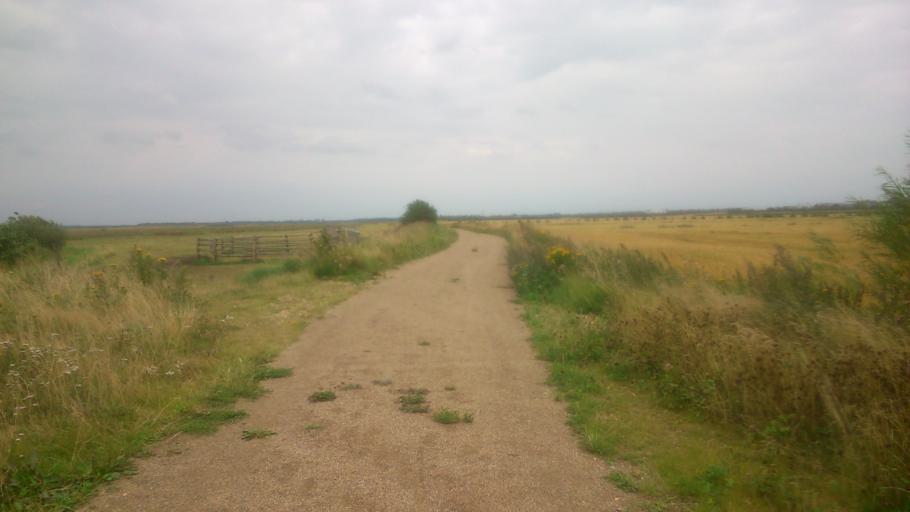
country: DK
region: Central Jutland
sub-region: Ringkobing-Skjern Kommune
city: Skjern
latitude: 55.9145
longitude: 8.4639
